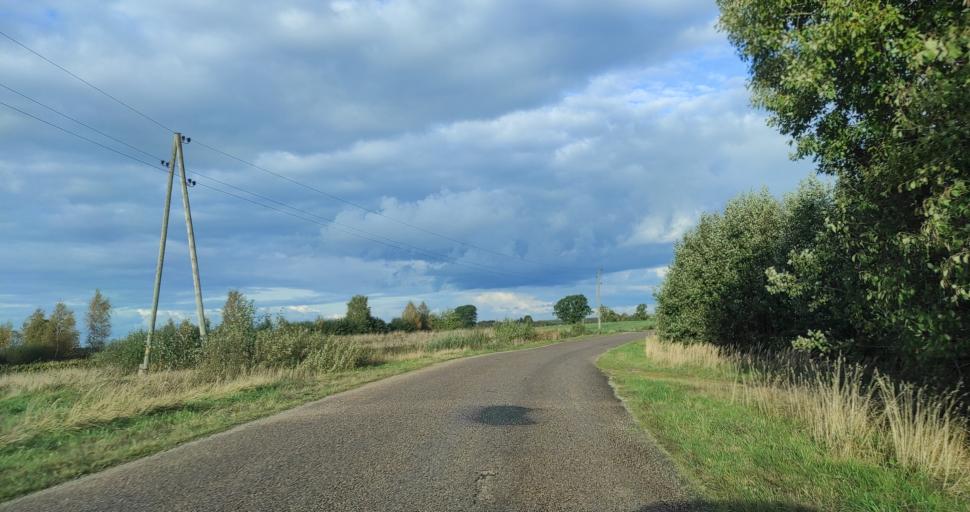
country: LV
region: Aizpute
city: Aizpute
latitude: 56.7807
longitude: 21.7706
